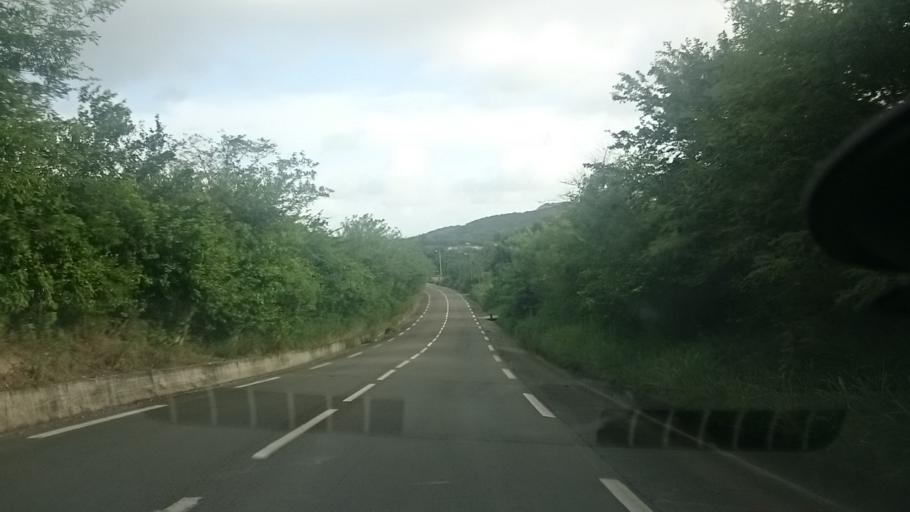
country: MQ
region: Martinique
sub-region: Martinique
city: Le Vauclin
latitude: 14.5376
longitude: -60.8400
